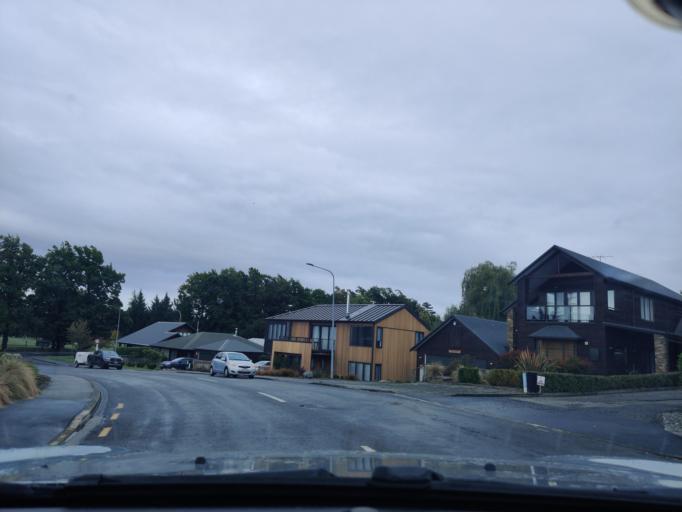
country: NZ
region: Canterbury
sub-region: Hurunui District
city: Amberley
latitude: -42.5199
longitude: 172.8269
